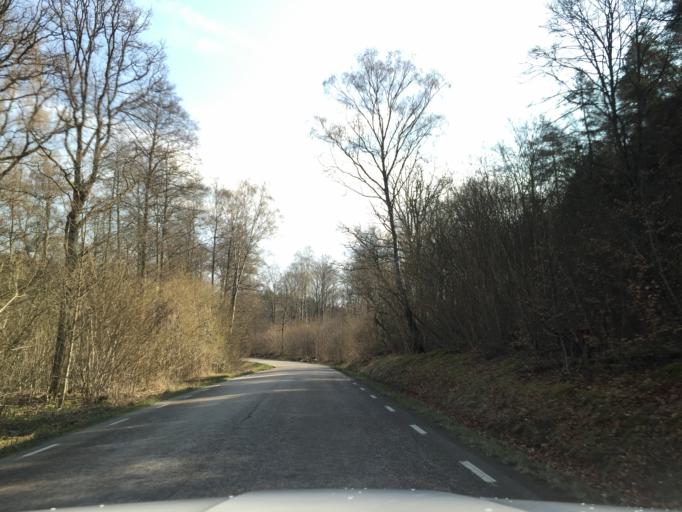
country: SE
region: Vaestra Goetaland
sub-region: Kungalvs Kommun
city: Kode
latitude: 57.9377
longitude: 11.8811
